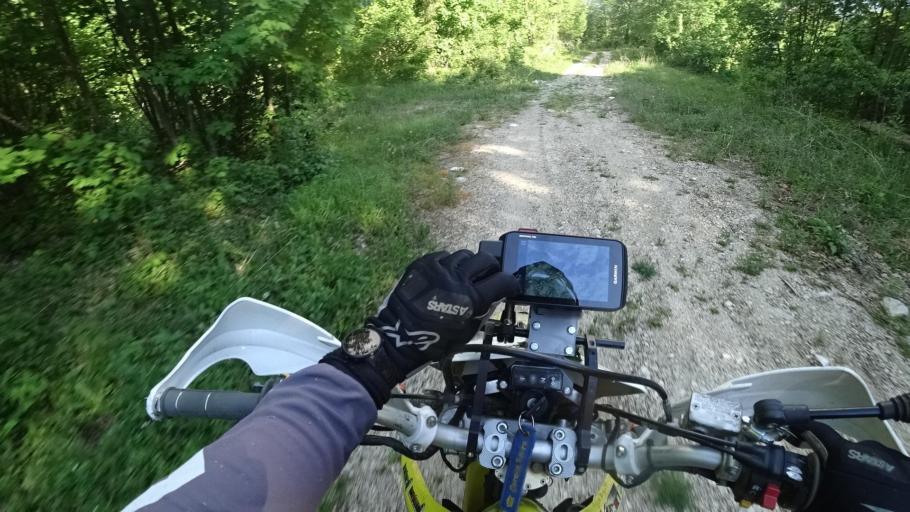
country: BA
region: Federation of Bosnia and Herzegovina
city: Sanica
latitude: 44.6617
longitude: 16.6033
